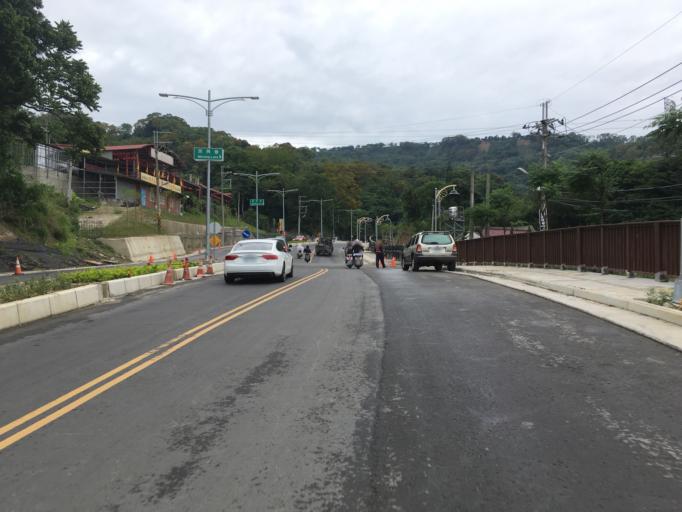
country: TW
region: Taiwan
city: Fengyuan
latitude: 24.2018
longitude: 120.7826
